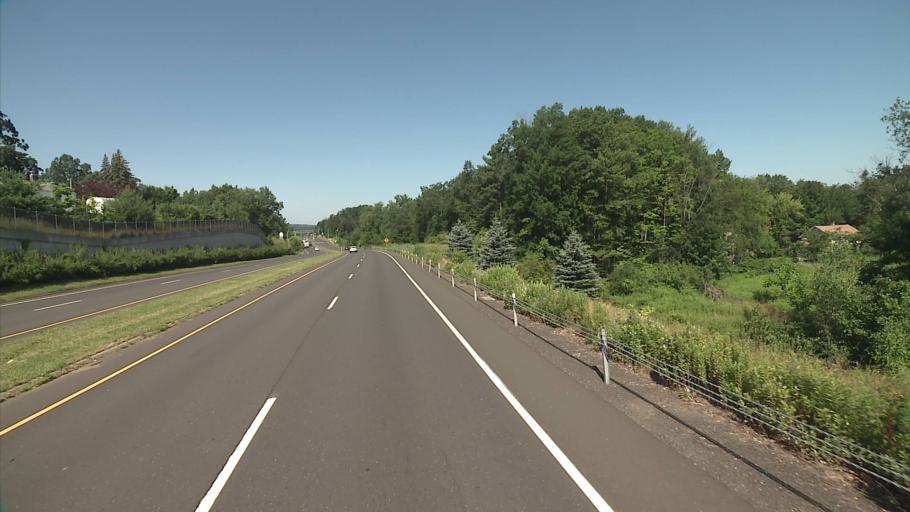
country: US
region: Connecticut
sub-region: Hartford County
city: Plainville
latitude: 41.6718
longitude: -72.8910
